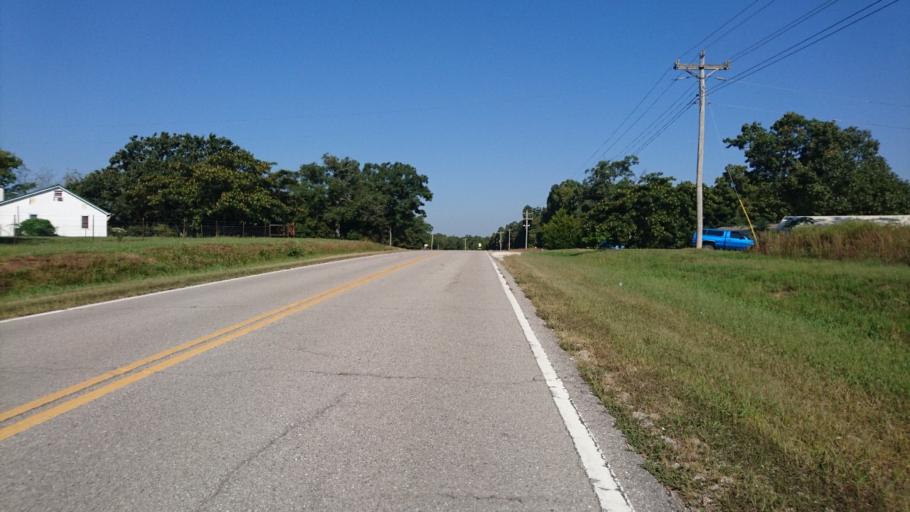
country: US
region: Missouri
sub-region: Pulaski County
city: Richland
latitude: 37.7480
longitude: -92.3602
